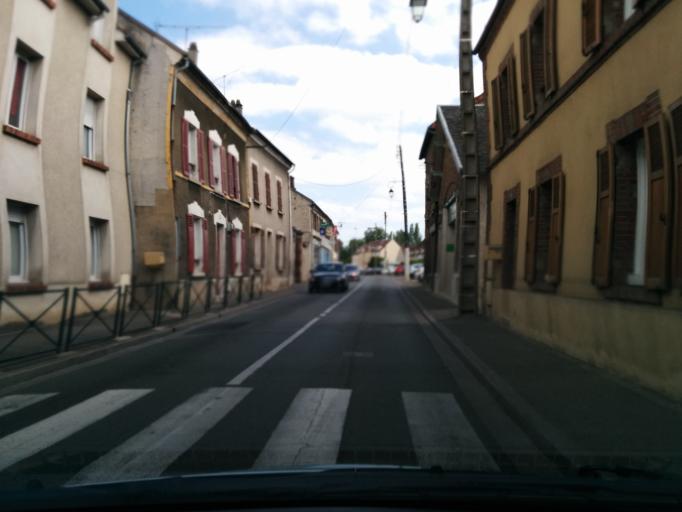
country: FR
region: Ile-de-France
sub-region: Departement des Yvelines
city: Maule
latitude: 48.9106
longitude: 1.8542
